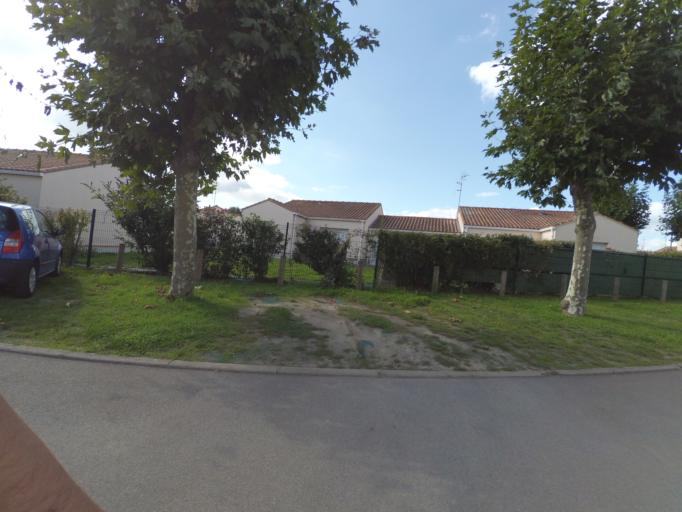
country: FR
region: Pays de la Loire
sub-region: Departement de la Loire-Atlantique
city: Chemere
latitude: 47.1170
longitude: -1.9170
